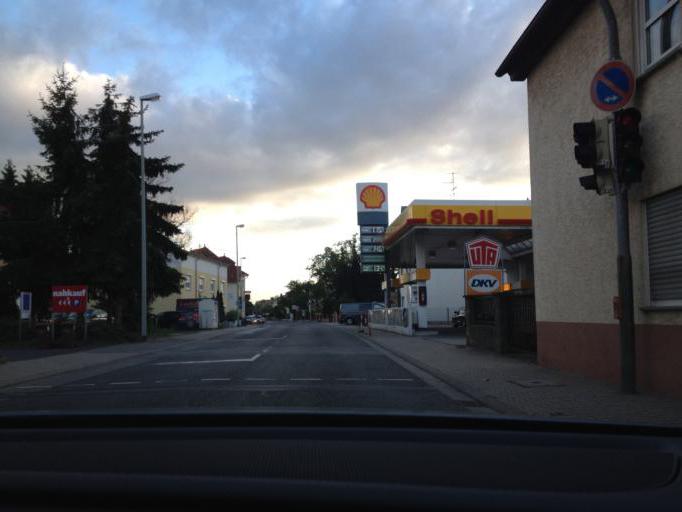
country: DE
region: Hesse
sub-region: Regierungsbezirk Darmstadt
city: Hochheim am Main
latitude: 50.0606
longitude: 8.3701
